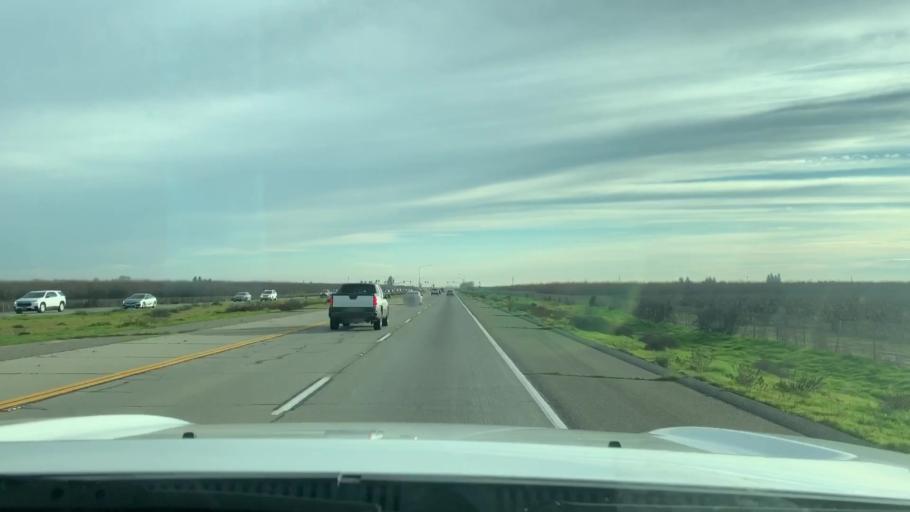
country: US
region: California
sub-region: Fresno County
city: Caruthers
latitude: 36.5235
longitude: -119.7864
